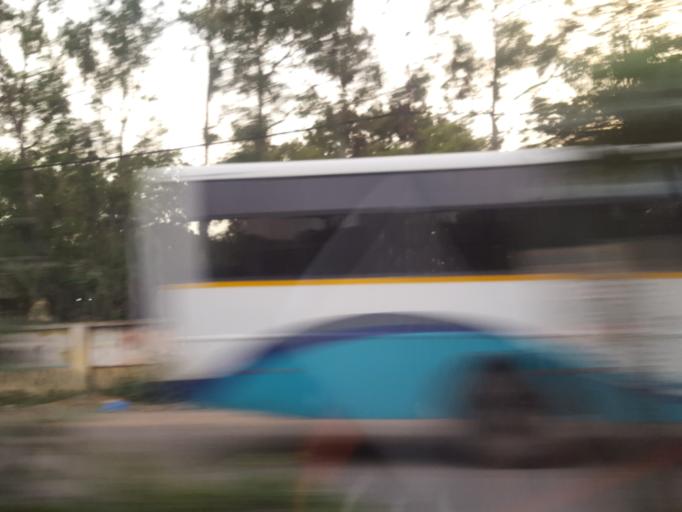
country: IN
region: Telangana
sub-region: Rangareddi
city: Kukatpalli
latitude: 17.5113
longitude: 78.3616
